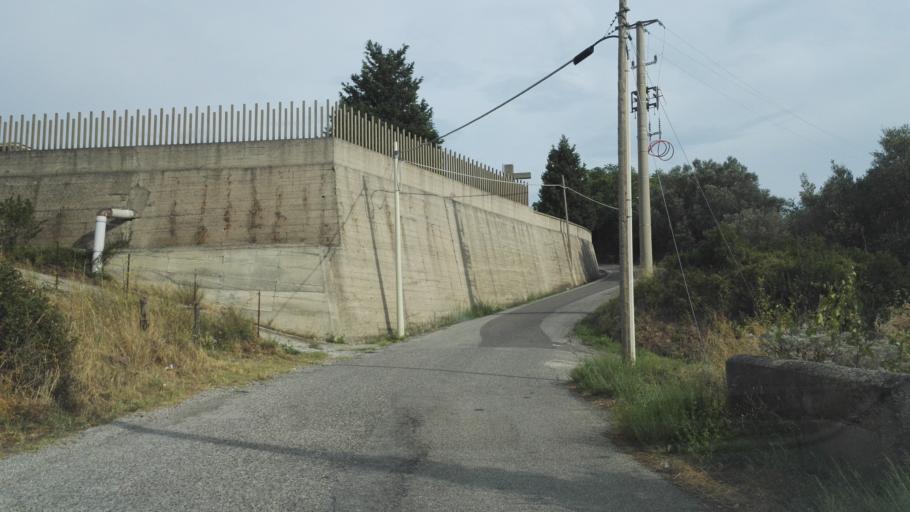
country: IT
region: Calabria
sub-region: Provincia di Reggio Calabria
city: Stignano
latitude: 38.4228
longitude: 16.4660
